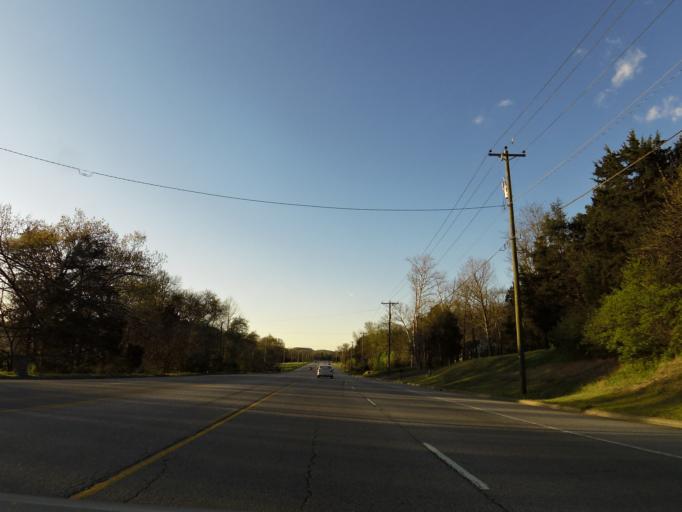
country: US
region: Tennessee
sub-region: Sumner County
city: Millersville
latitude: 36.3495
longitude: -86.7218
